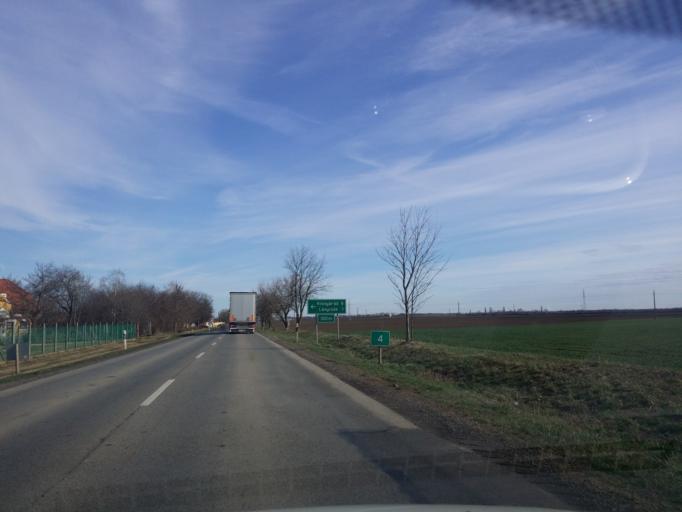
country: HU
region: Baranya
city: Lanycsok
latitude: 45.9999
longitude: 18.6280
